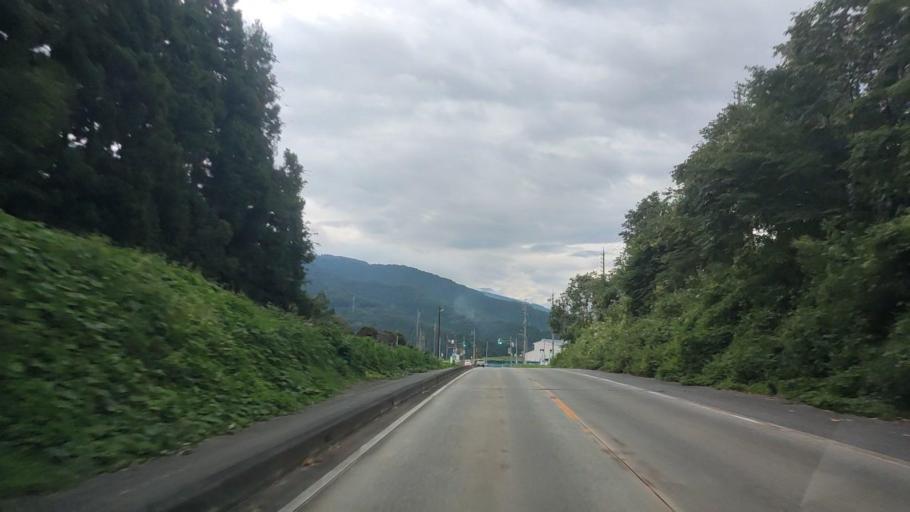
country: JP
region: Nagano
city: Iiyama
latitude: 36.8877
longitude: 138.4094
